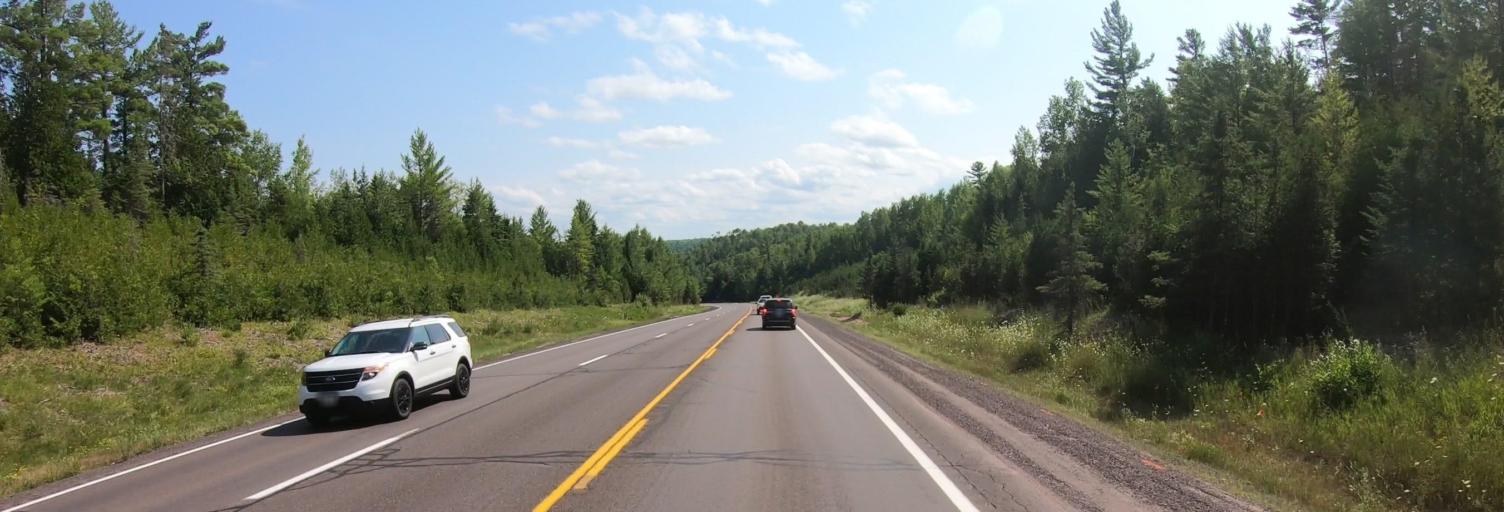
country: US
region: Michigan
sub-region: Ontonagon County
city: Ontonagon
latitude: 46.7110
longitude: -89.1598
